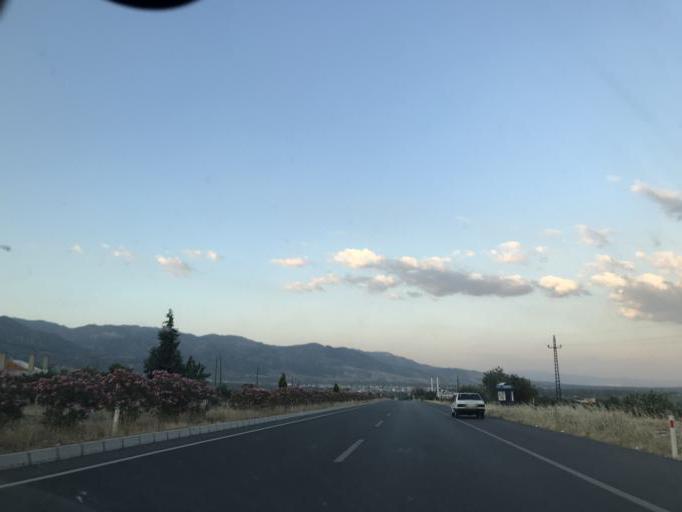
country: TR
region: Aydin
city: Buharkent
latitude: 37.9555
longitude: 28.6997
